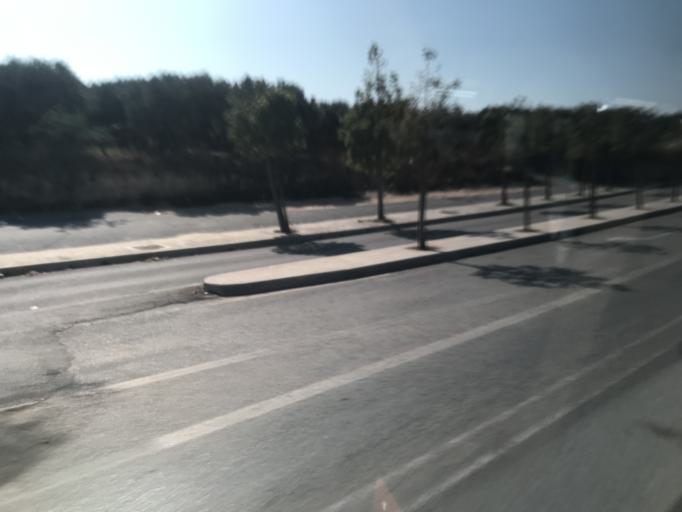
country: GR
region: Crete
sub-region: Nomos Irakleiou
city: Gazi
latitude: 35.3058
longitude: 25.0866
